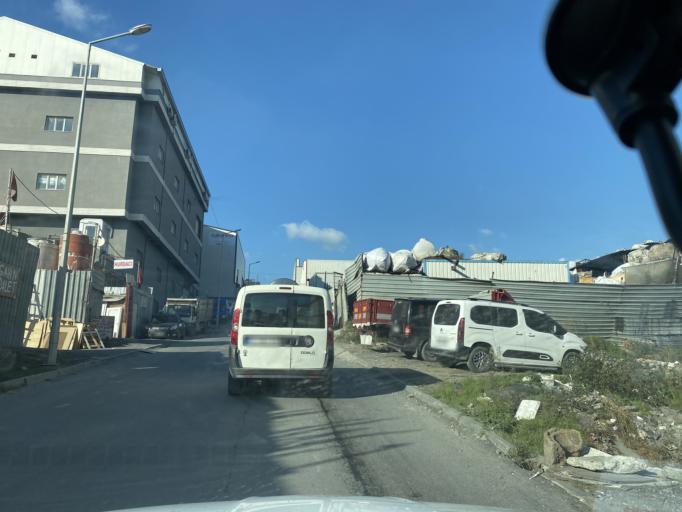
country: TR
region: Istanbul
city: Esenyurt
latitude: 41.0528
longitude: 28.6480
